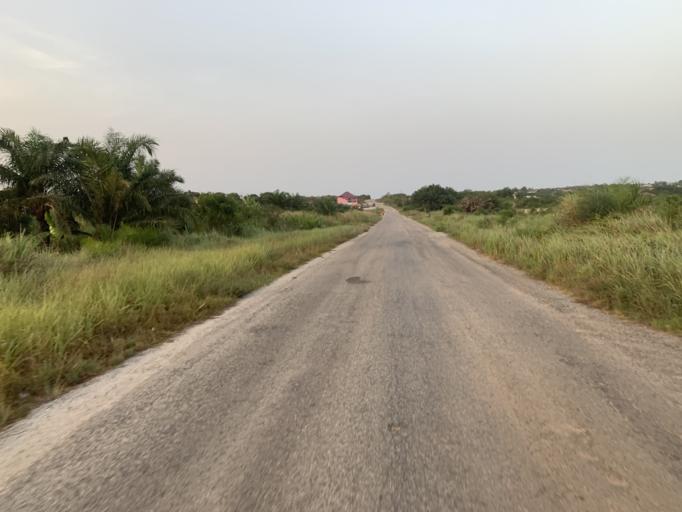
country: GH
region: Central
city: Winneba
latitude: 5.3743
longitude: -0.6134
